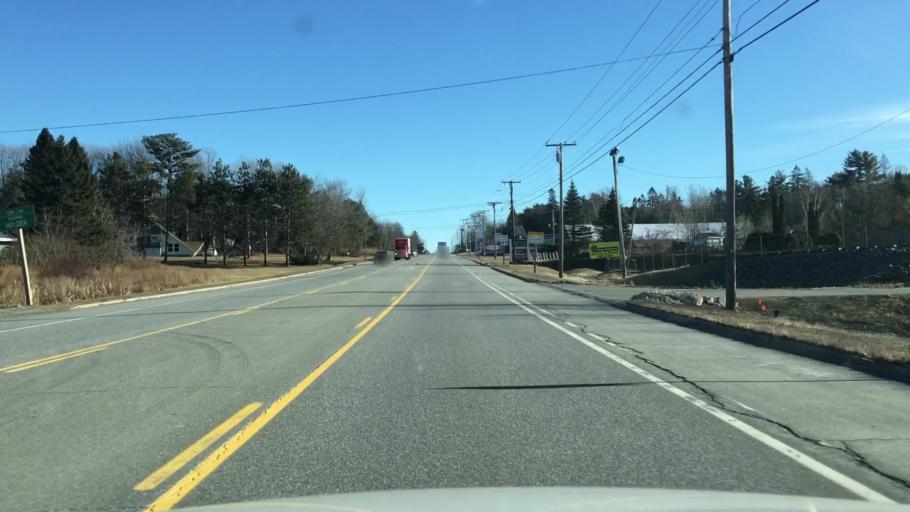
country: US
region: Maine
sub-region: Penobscot County
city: Holden
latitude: 44.7678
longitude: -68.7133
